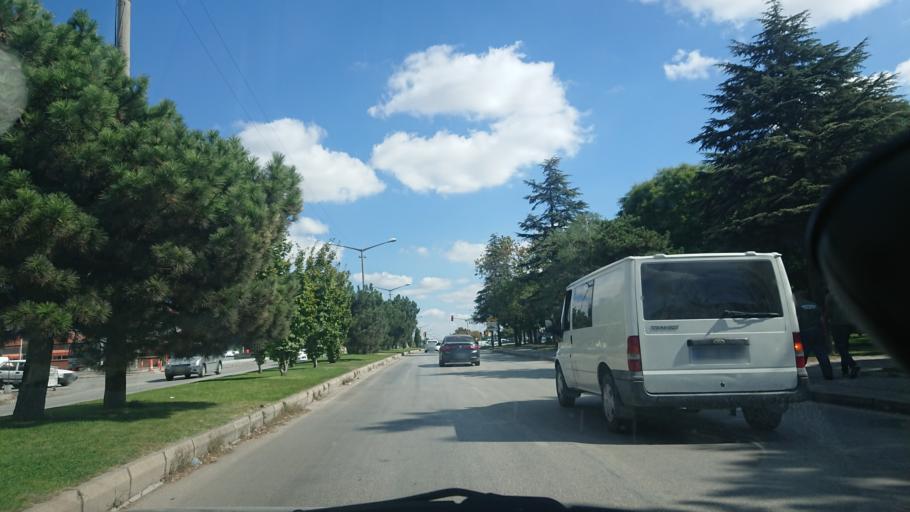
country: TR
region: Eskisehir
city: Eskisehir
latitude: 39.7636
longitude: 30.5578
